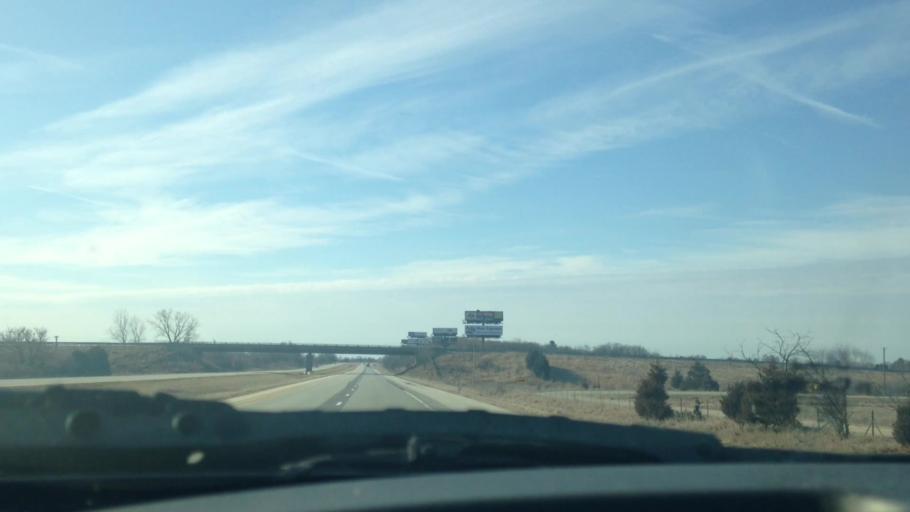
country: US
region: Illinois
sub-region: Ford County
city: Paxton
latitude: 40.5195
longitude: -88.0848
